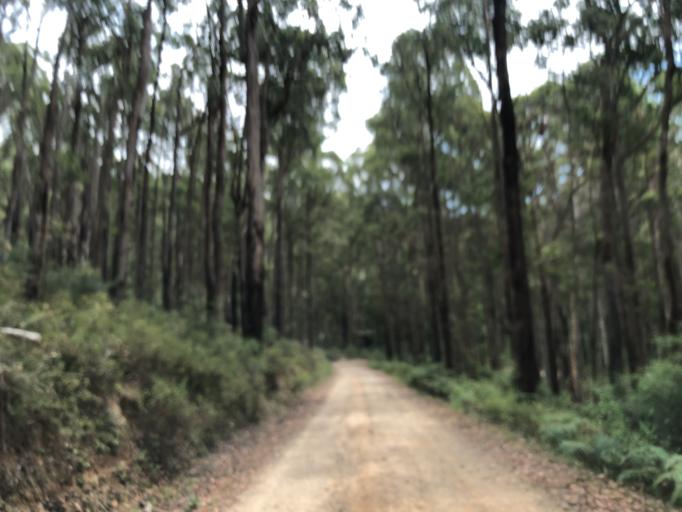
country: AU
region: Victoria
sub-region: Moorabool
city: Bacchus Marsh
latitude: -37.4581
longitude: 144.2696
